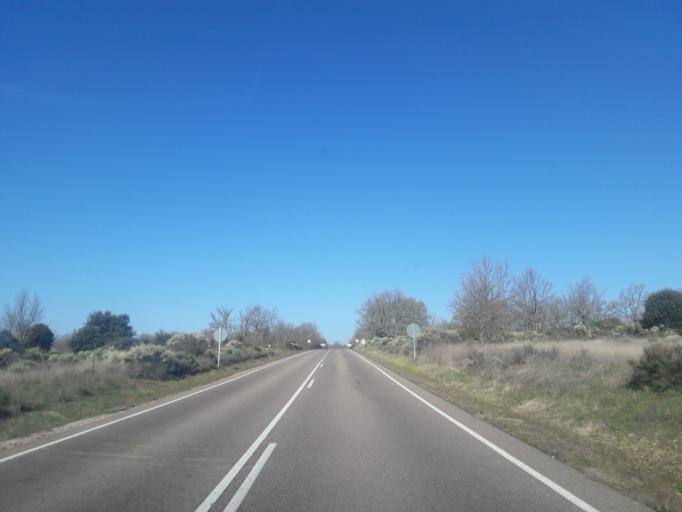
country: ES
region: Castille and Leon
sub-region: Provincia de Salamanca
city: Villasbuenas
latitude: 41.0792
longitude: -6.5575
